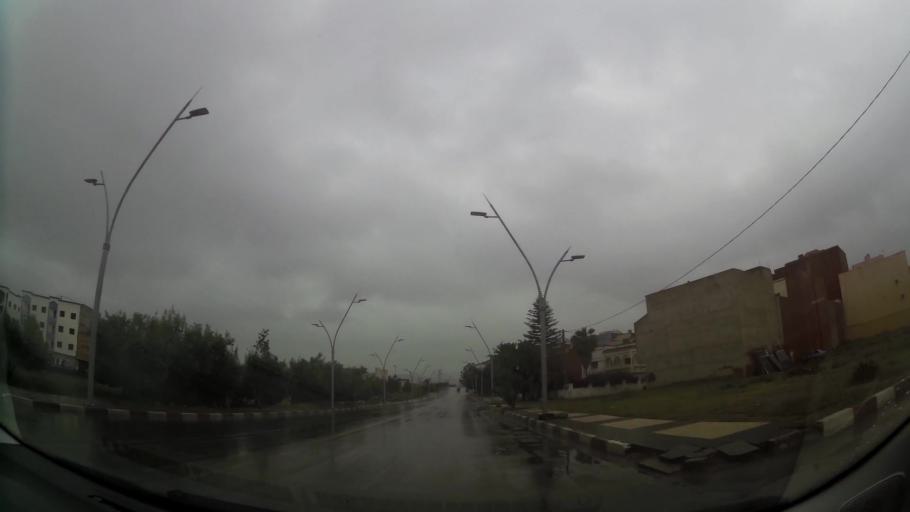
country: MA
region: Oriental
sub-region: Nador
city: Nador
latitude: 35.1580
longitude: -2.9724
